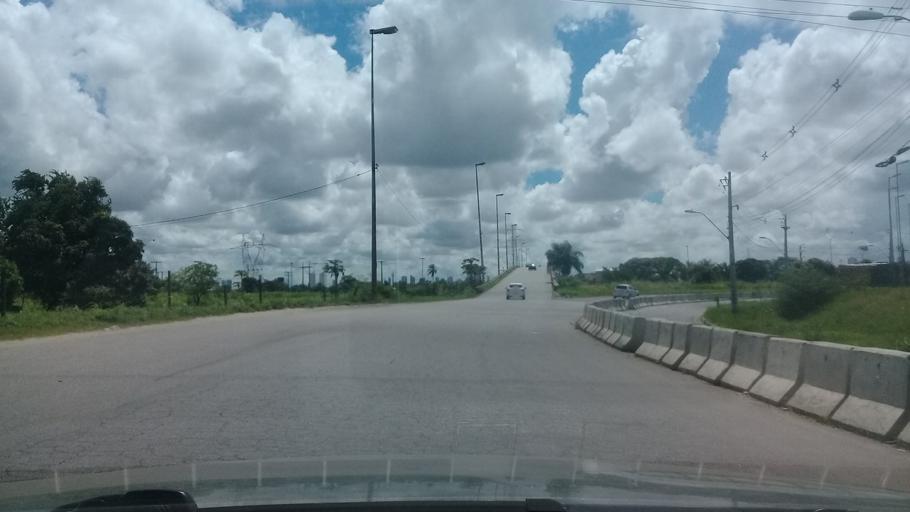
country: BR
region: Pernambuco
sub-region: Recife
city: Recife
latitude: -8.0704
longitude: -34.9422
